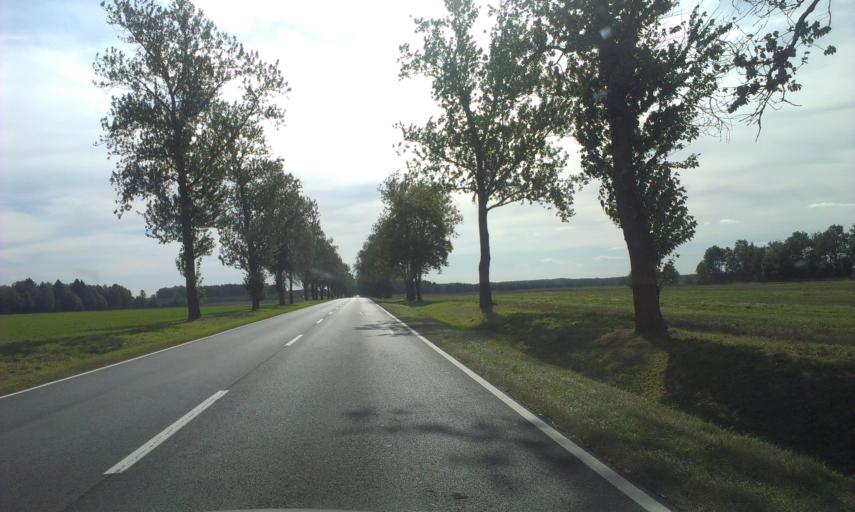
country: PL
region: Greater Poland Voivodeship
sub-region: Powiat zlotowski
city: Okonek
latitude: 53.5834
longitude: 16.8214
